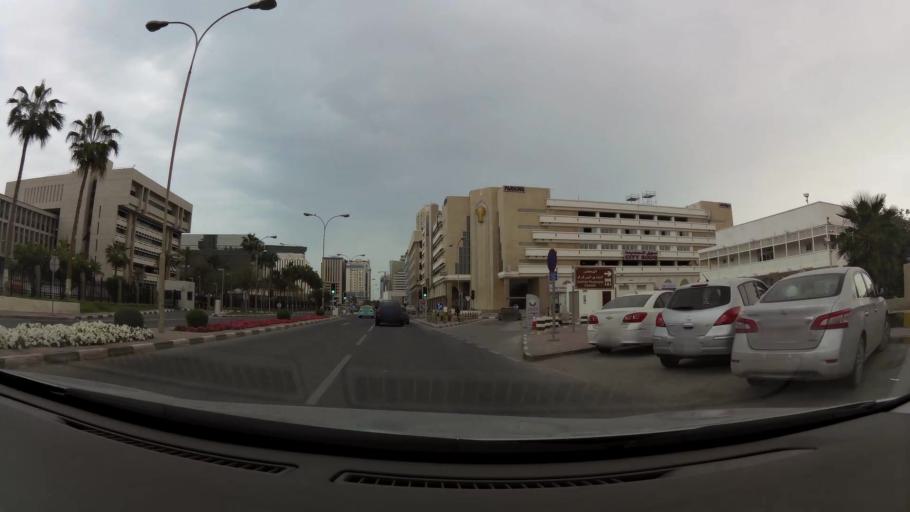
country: QA
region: Baladiyat ad Dawhah
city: Doha
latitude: 25.2894
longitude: 51.5368
